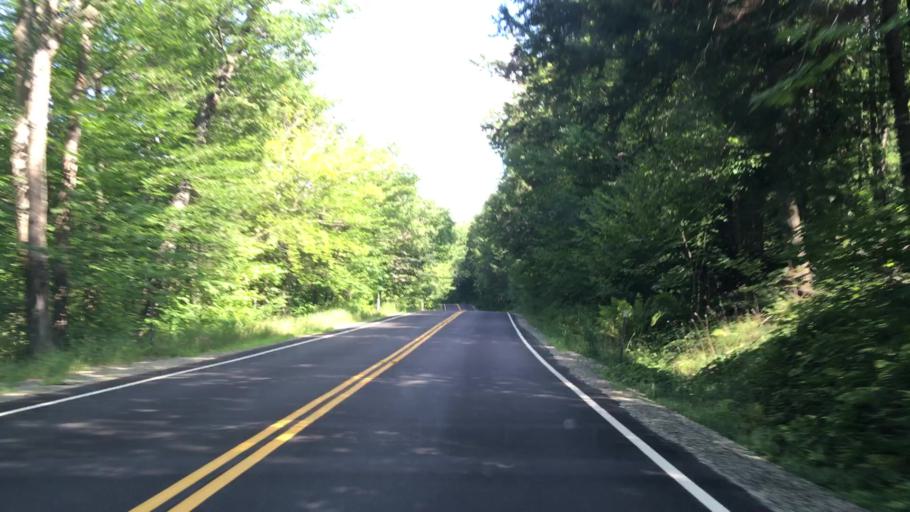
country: US
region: New Hampshire
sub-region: Grafton County
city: North Haverhill
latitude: 44.1083
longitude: -71.8983
